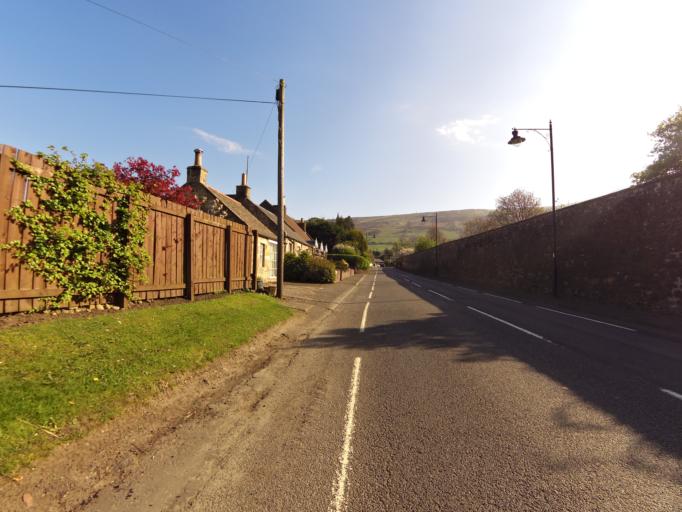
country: GB
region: Scotland
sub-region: Fife
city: Falkland
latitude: 56.2549
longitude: -3.2049
